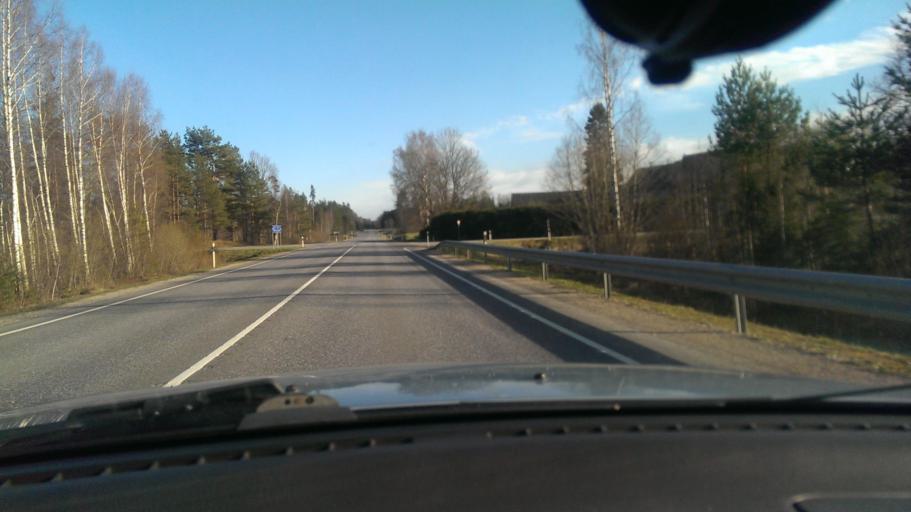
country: EE
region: Tartu
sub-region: UElenurme vald
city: Ulenurme
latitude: 58.1163
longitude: 26.7343
